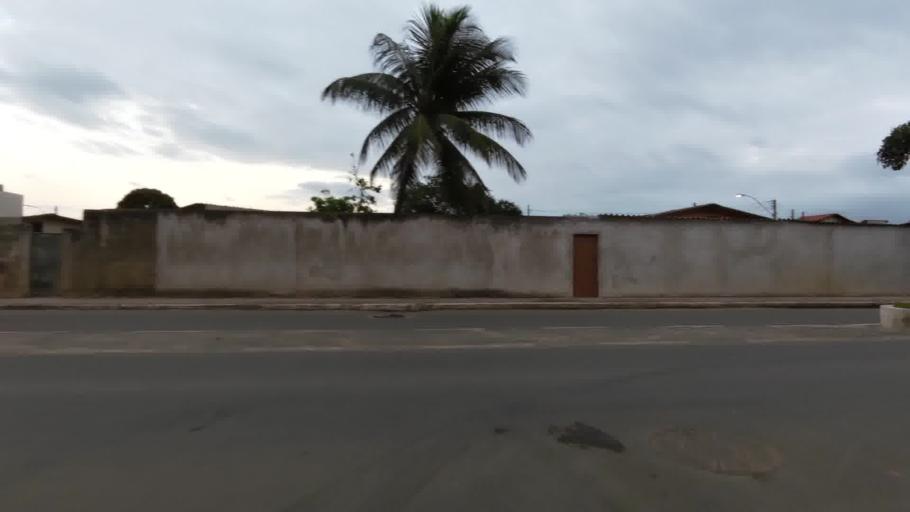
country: BR
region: Espirito Santo
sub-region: Piuma
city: Piuma
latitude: -20.8095
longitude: -40.6384
